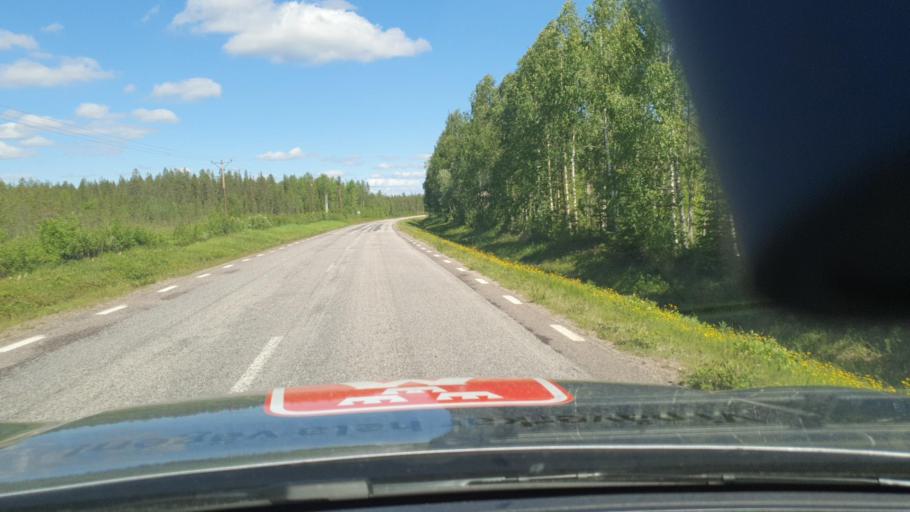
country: SE
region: Norrbotten
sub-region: Overkalix Kommun
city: OEverkalix
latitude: 67.0378
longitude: 22.5026
